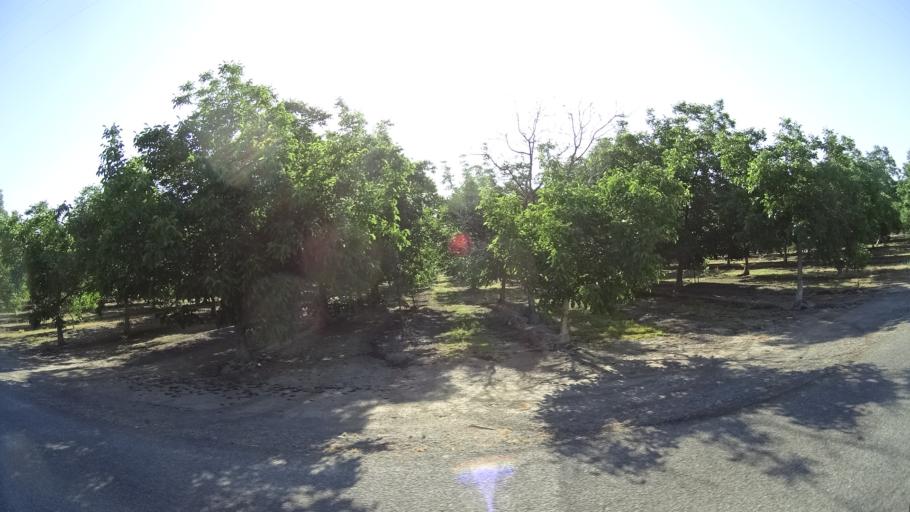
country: US
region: California
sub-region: Fresno County
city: Laton
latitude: 36.4041
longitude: -119.7134
